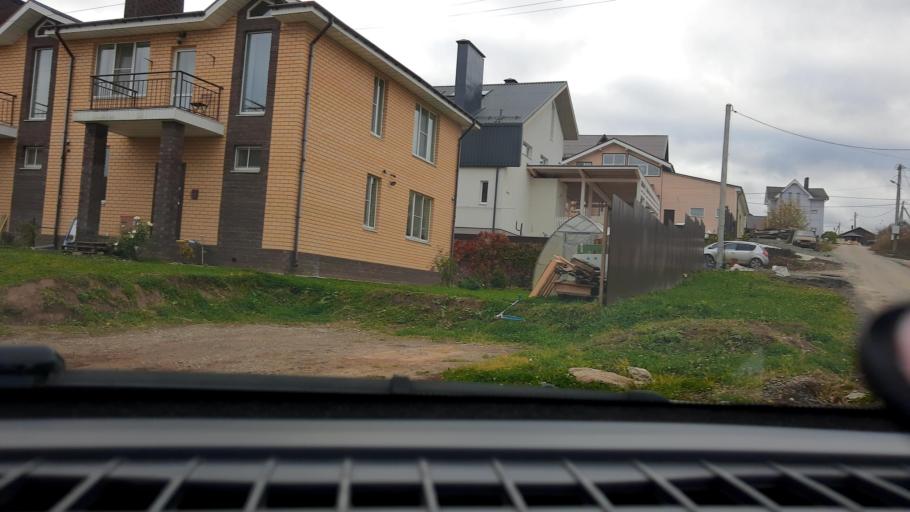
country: RU
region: Nizjnij Novgorod
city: Afonino
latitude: 56.2654
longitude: 44.0686
